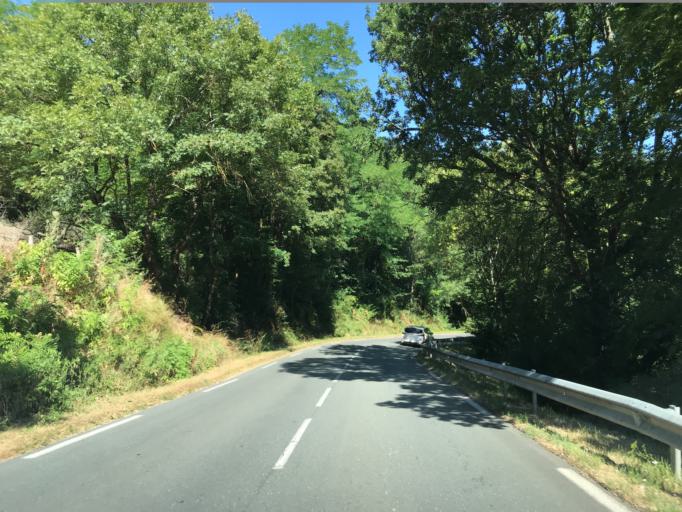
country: FR
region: Limousin
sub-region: Departement de la Correze
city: Larche
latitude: 45.1046
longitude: 1.3851
